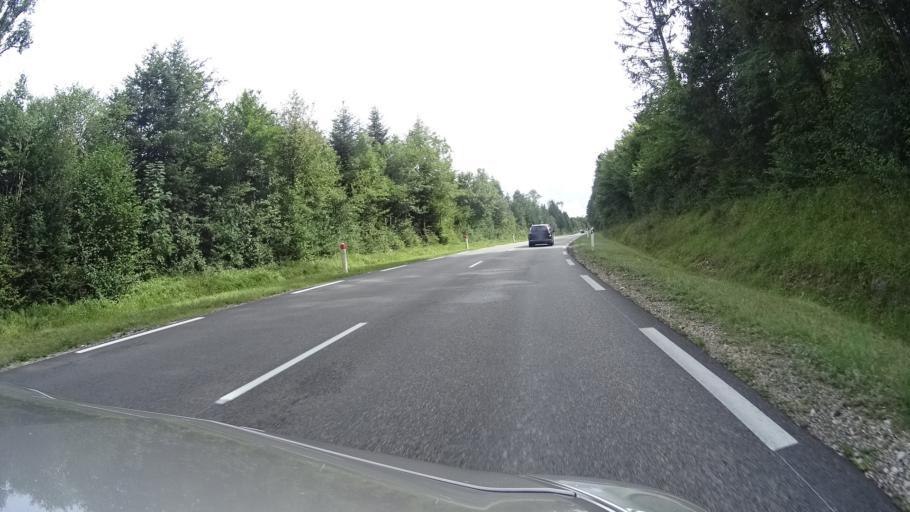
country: FR
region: Franche-Comte
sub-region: Departement du Jura
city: Champagnole
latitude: 46.7087
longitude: 5.9306
